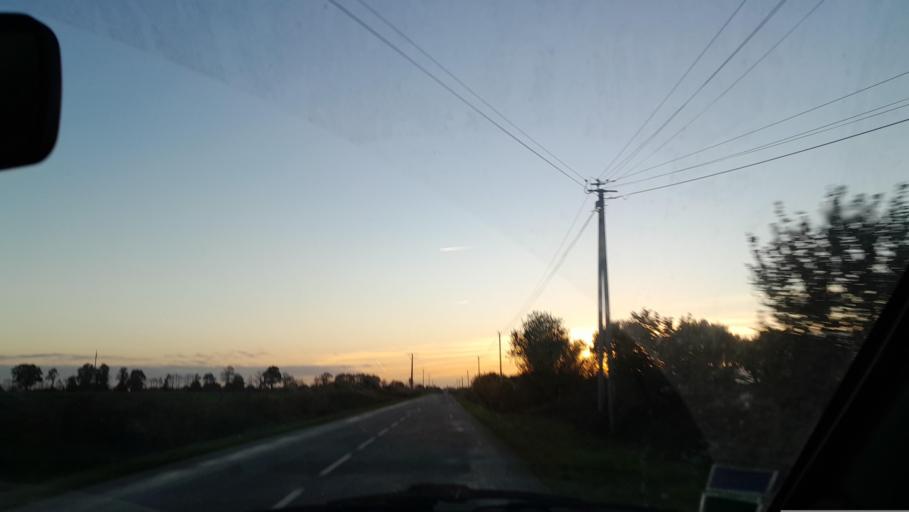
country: FR
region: Pays de la Loire
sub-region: Departement de la Mayenne
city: Ballots
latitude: 47.9531
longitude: -1.0653
